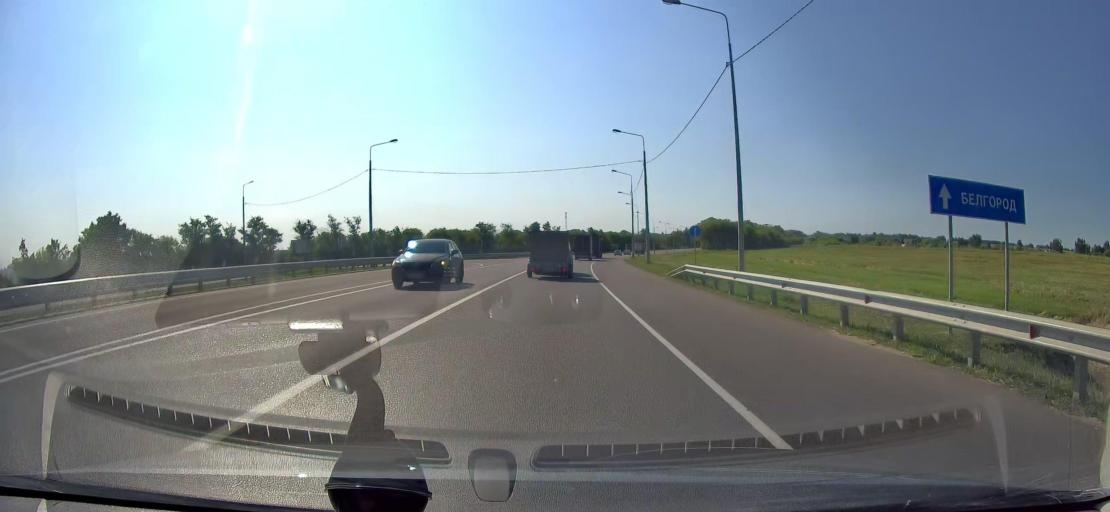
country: RU
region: Orjol
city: Kromy
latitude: 52.6468
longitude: 35.7430
